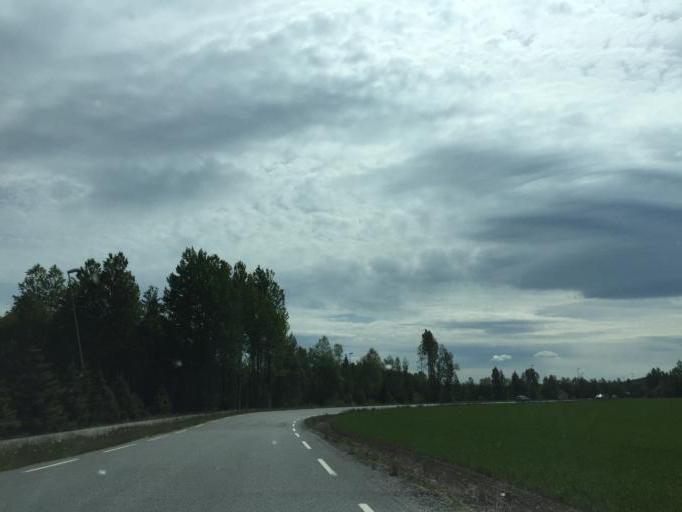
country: NO
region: Akershus
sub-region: Nes
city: Fjellfoten
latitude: 60.1028
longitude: 11.4814
